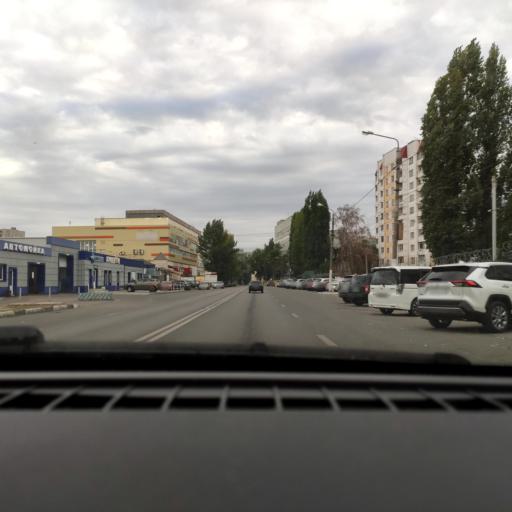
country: RU
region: Voronezj
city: Voronezh
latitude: 51.6774
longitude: 39.2519
